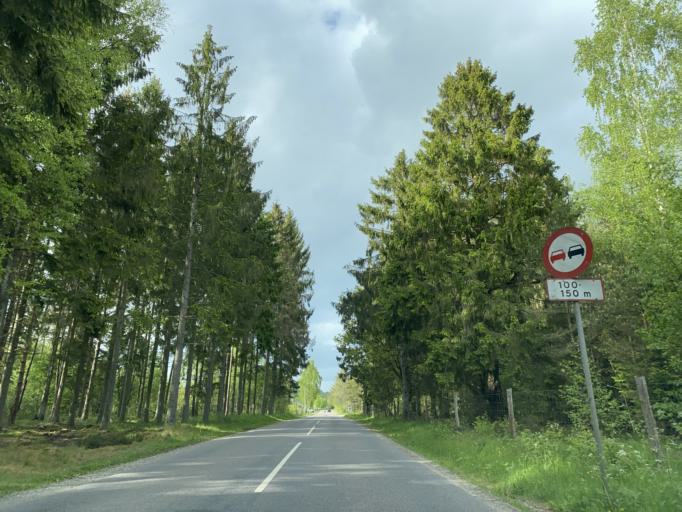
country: DK
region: Central Jutland
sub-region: Skanderborg Kommune
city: Ry
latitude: 56.0639
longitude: 9.6929
